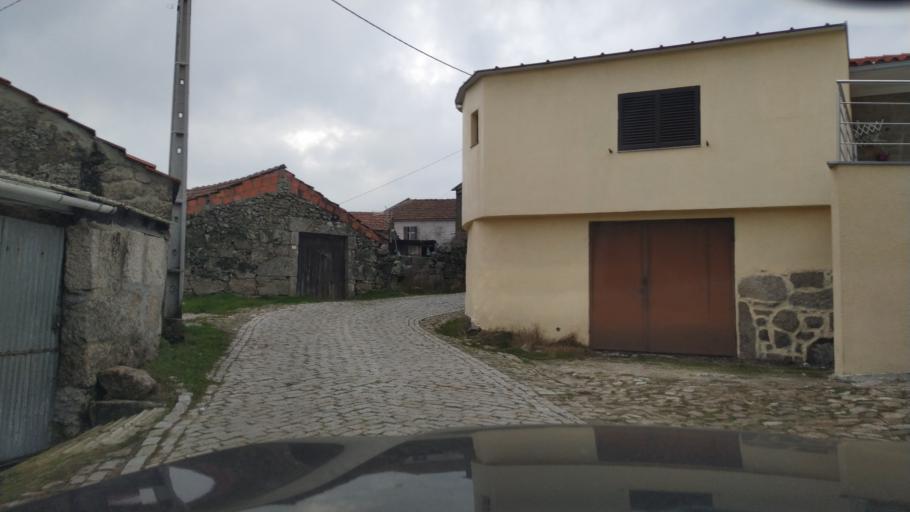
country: PT
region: Vila Real
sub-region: Sabrosa
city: Sabrosa
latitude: 41.3316
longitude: -7.6307
